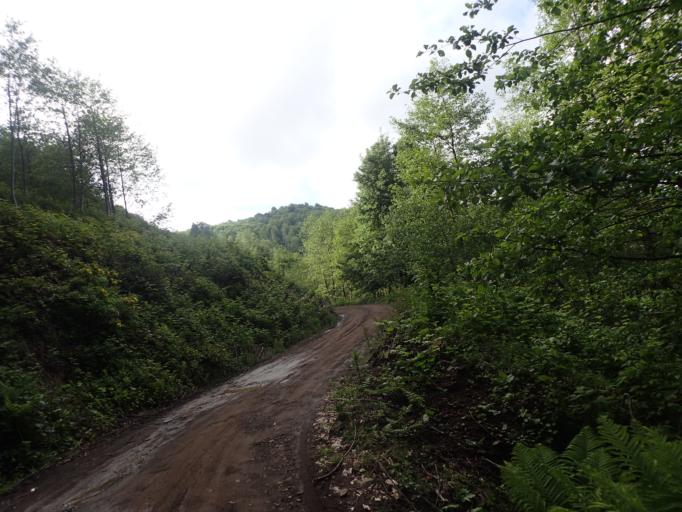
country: TR
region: Samsun
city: Salipazari
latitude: 40.9428
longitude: 36.8786
